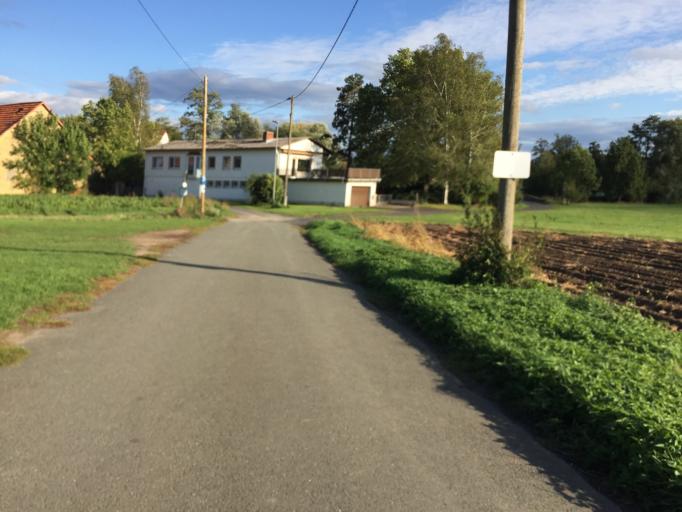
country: DE
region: Hesse
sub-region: Regierungsbezirk Darmstadt
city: Munzenberg
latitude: 50.4610
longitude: 8.7521
